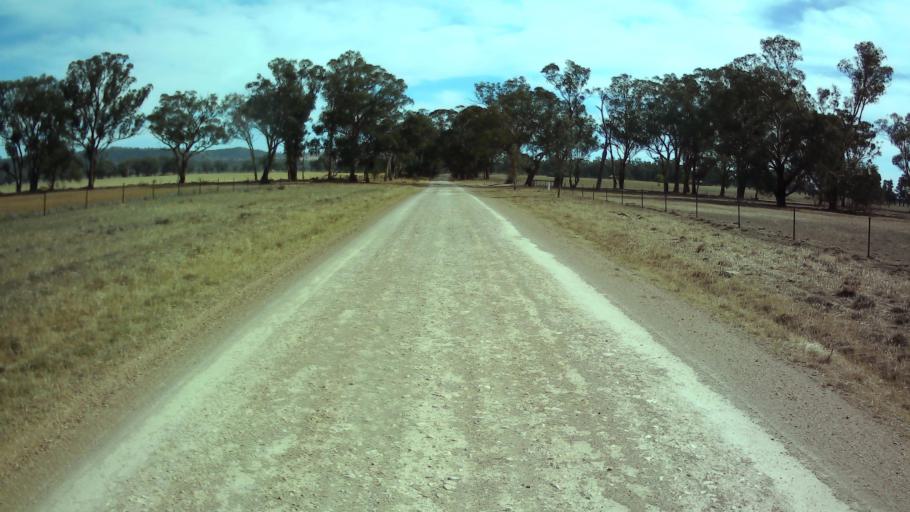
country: AU
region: New South Wales
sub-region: Weddin
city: Grenfell
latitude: -33.7007
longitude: 148.3022
